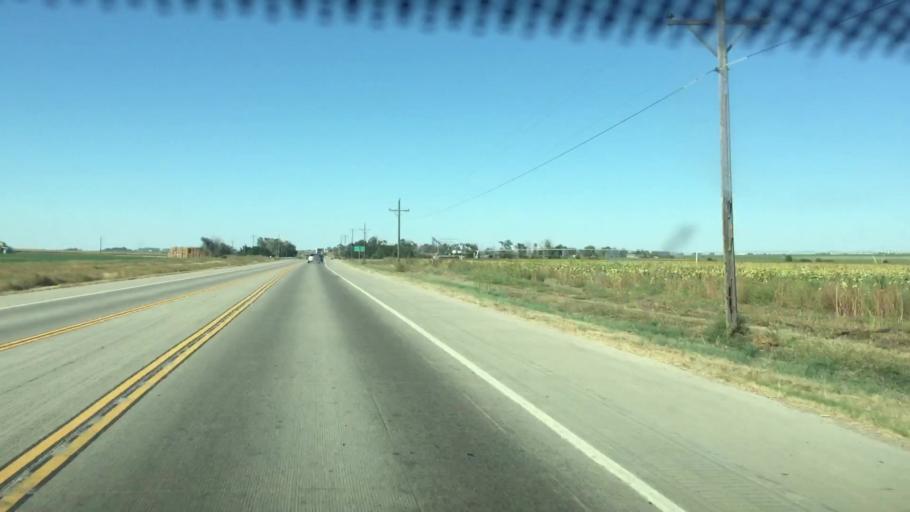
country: US
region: Colorado
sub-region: Prowers County
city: Lamar
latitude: 38.1610
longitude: -102.7238
